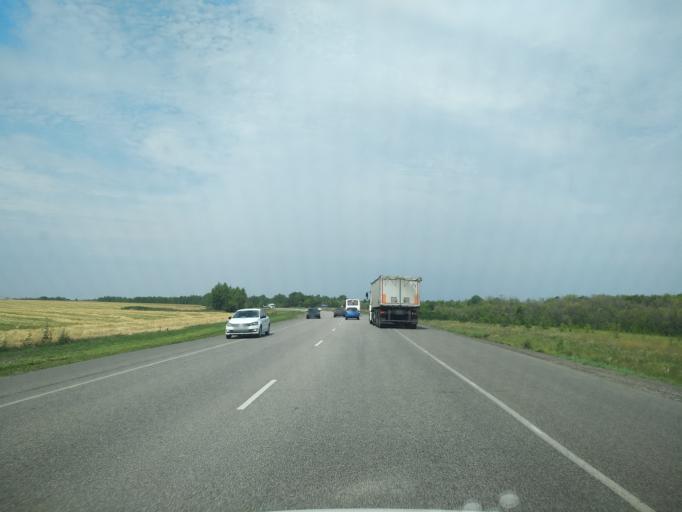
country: RU
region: Voronezj
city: Novaya Usman'
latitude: 51.7001
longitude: 39.4265
